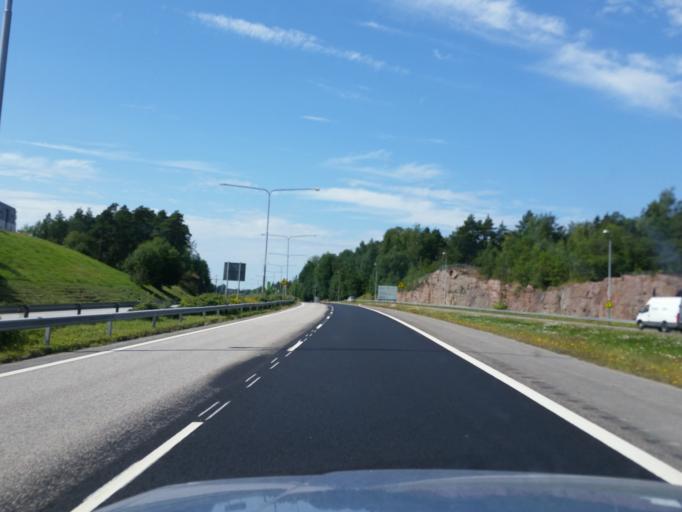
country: FI
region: Uusimaa
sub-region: Helsinki
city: Koukkuniemi
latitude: 60.1659
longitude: 24.7493
